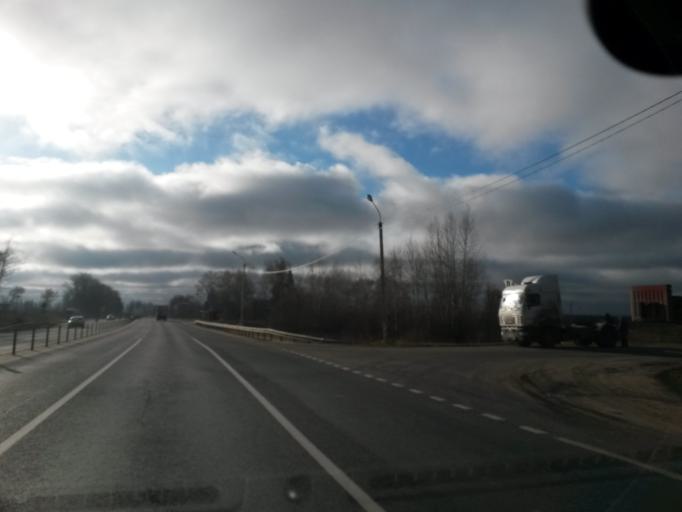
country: RU
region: Jaroslavl
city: Semibratovo
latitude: 57.3447
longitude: 39.5825
